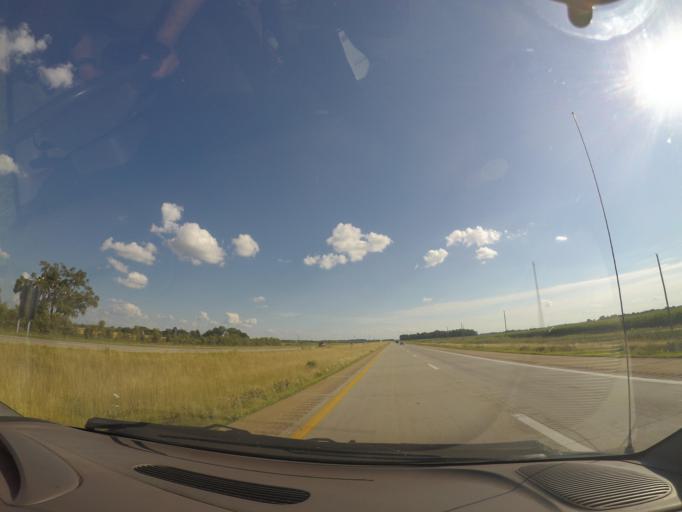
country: US
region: Ohio
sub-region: Lucas County
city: Whitehouse
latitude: 41.4915
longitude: -83.7686
